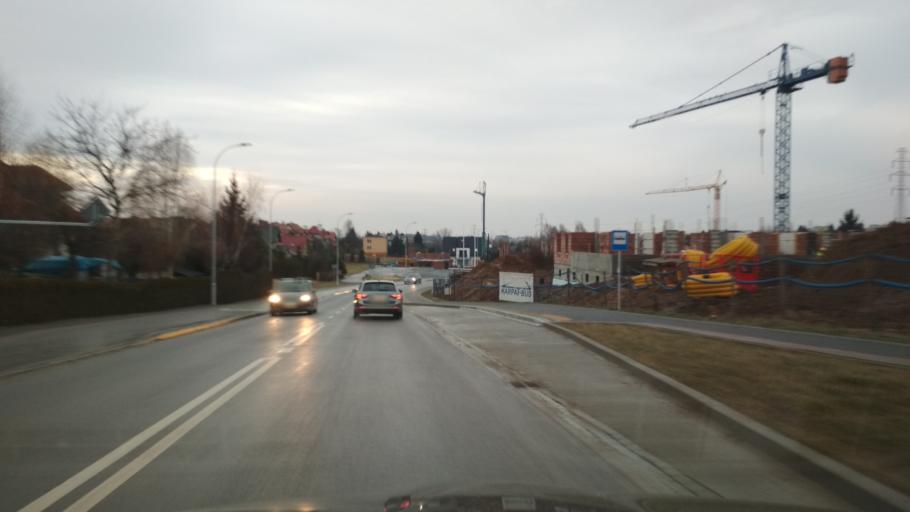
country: PL
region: Subcarpathian Voivodeship
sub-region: Rzeszow
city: Przybyszowka
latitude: 50.0452
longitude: 21.9611
